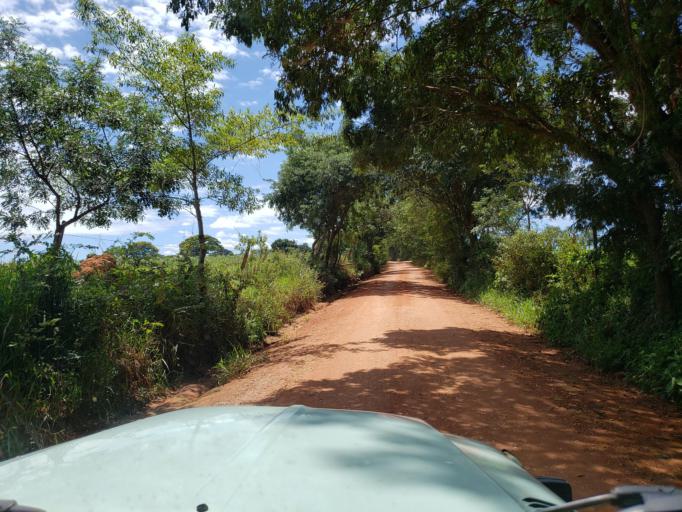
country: BR
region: Sao Paulo
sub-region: Moji-Guacu
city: Mogi-Gaucu
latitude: -22.2978
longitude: -46.8851
